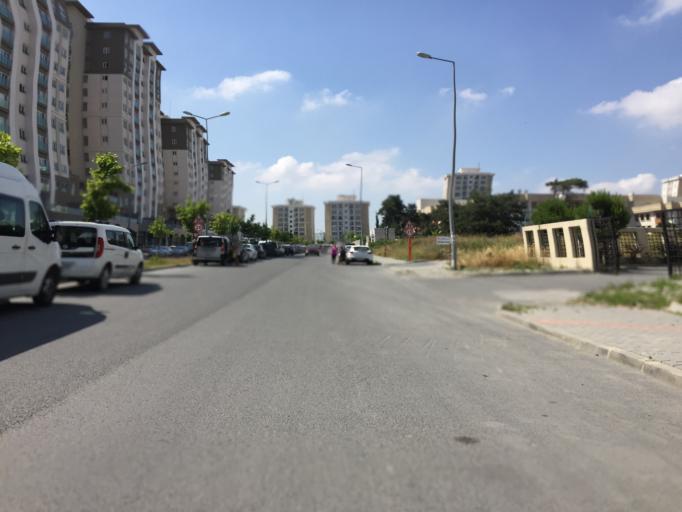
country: TR
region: Istanbul
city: Esenyurt
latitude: 41.0861
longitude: 28.6550
